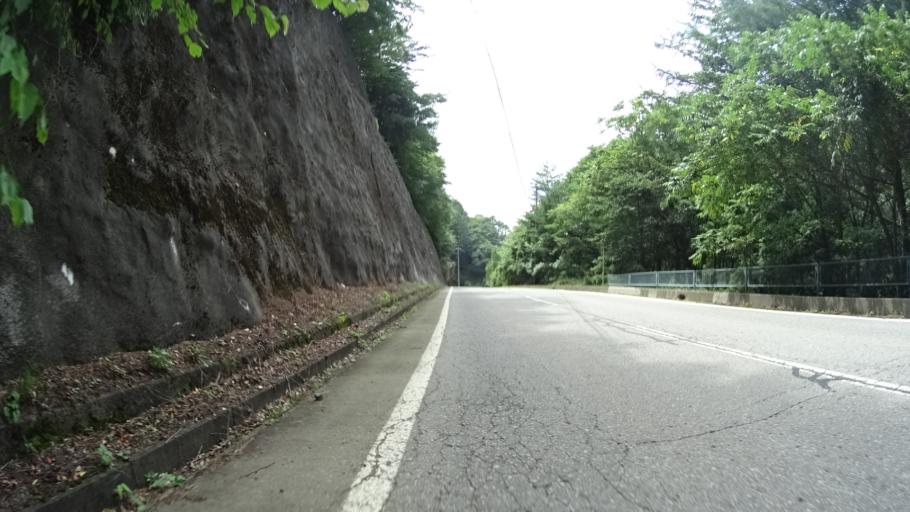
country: JP
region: Nagano
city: Saku
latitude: 36.0602
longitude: 138.5801
